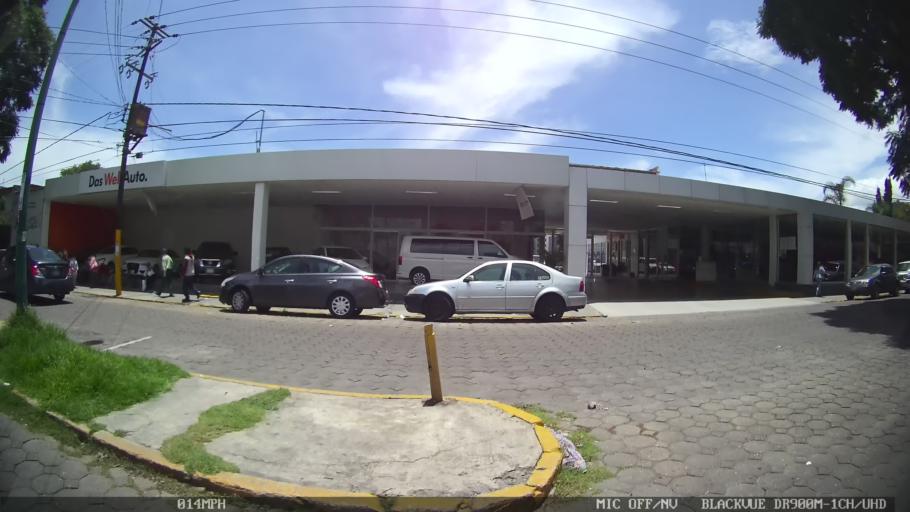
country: MX
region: Puebla
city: Puebla
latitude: 19.0539
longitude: -98.1994
